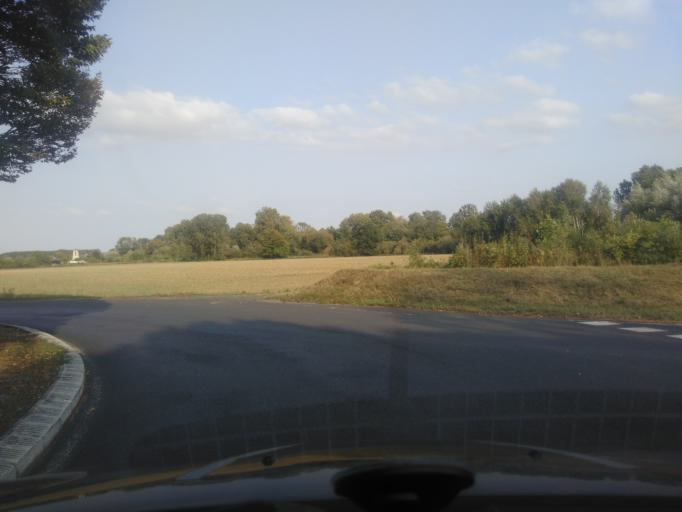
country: FR
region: Picardie
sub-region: Departement de l'Aisne
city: Laon
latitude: 49.5466
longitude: 3.6165
